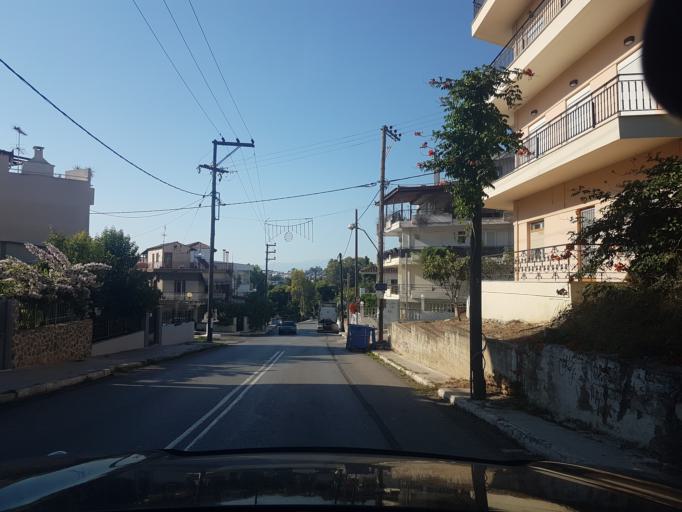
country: GR
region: Central Greece
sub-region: Nomos Evvoias
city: Chalkida
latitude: 38.4691
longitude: 23.5868
